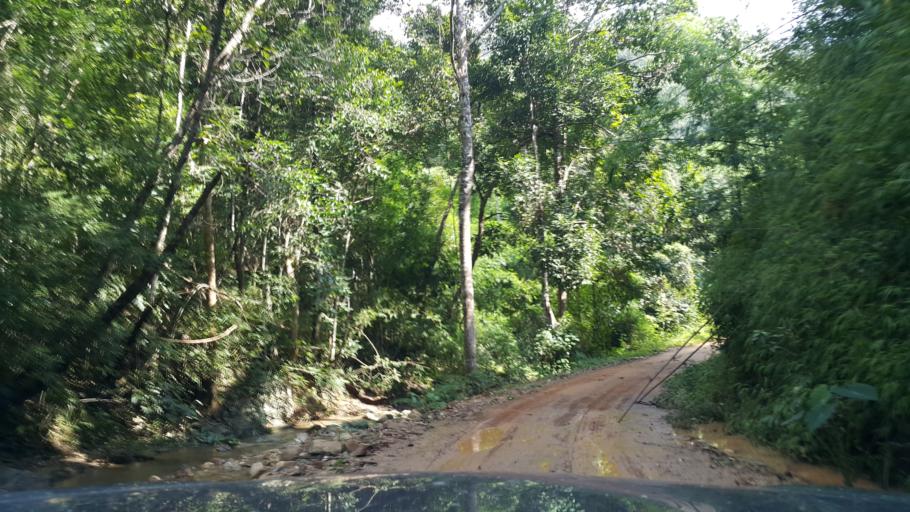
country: TH
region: Chiang Mai
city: Phrao
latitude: 19.0873
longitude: 99.2567
